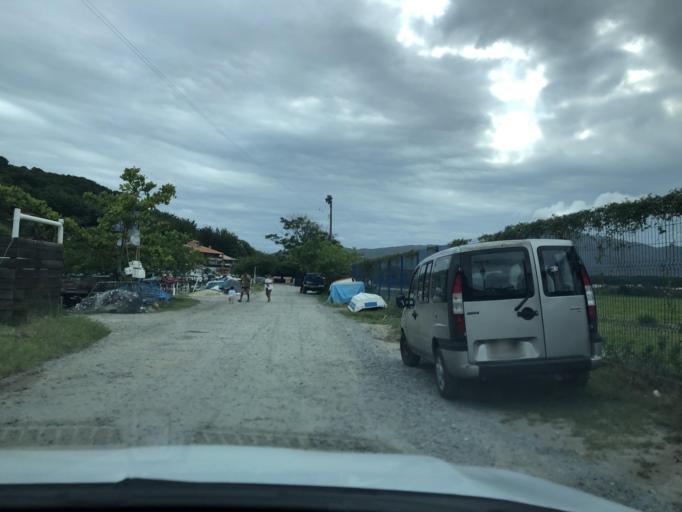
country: BR
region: Santa Catarina
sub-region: Florianopolis
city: Lagoa
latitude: -27.5782
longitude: -48.4257
